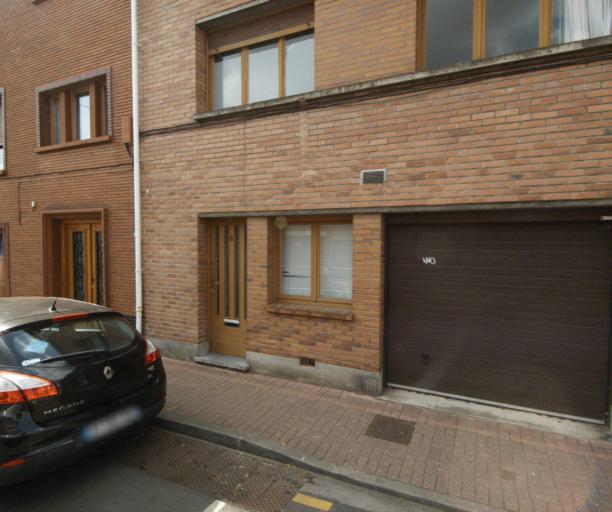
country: FR
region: Nord-Pas-de-Calais
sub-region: Departement du Nord
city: La Madeleine
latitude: 50.6479
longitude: 3.0895
